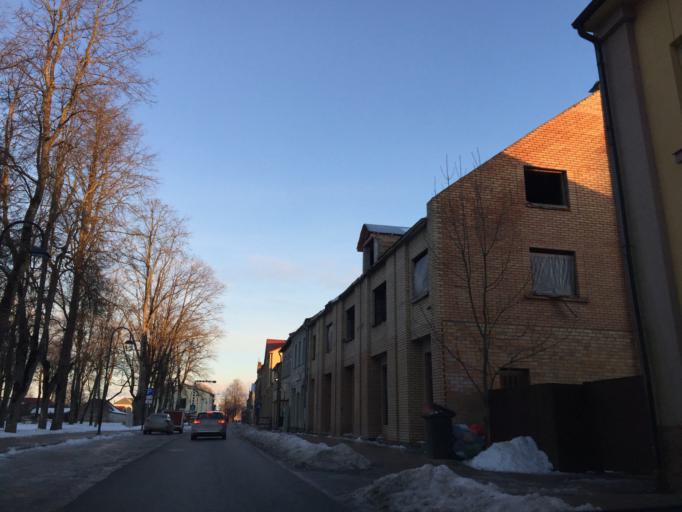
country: LV
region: Jaunjelgava
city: Jaunjelgava
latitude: 56.6169
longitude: 25.0807
